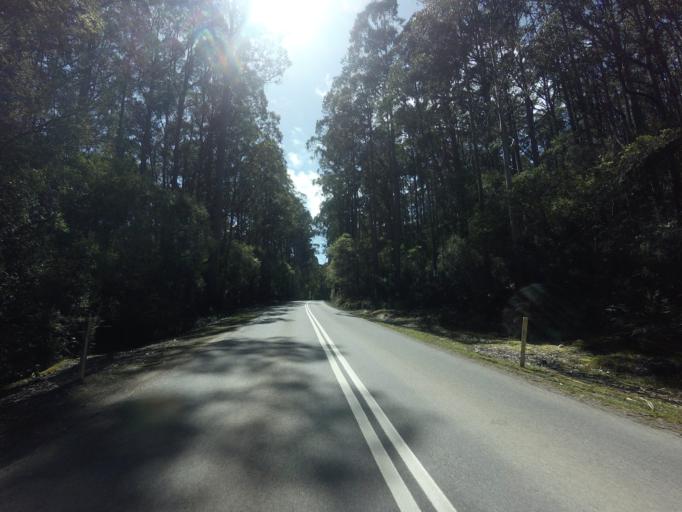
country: AU
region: Tasmania
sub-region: Derwent Valley
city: New Norfolk
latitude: -42.7334
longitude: 146.6662
